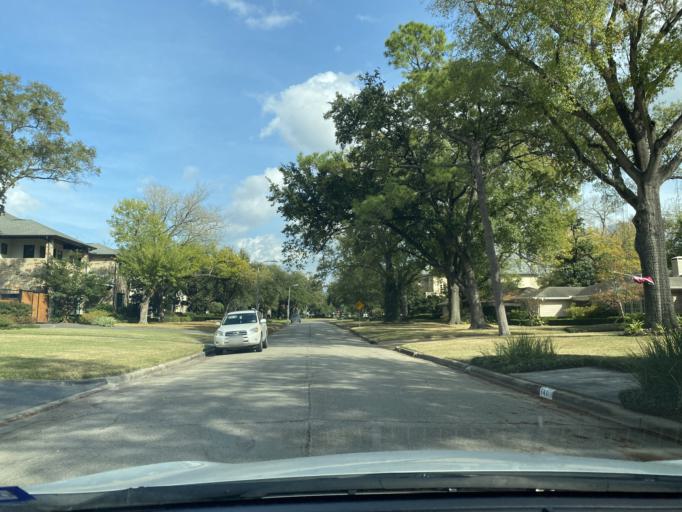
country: US
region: Texas
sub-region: Harris County
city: Hunters Creek Village
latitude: 29.7523
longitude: -95.4707
